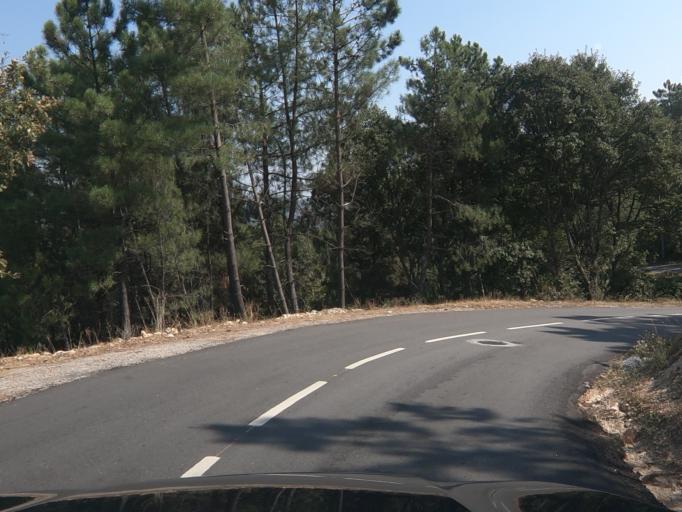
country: PT
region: Vila Real
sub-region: Sabrosa
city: Sabrosa
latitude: 41.3169
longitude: -7.5879
